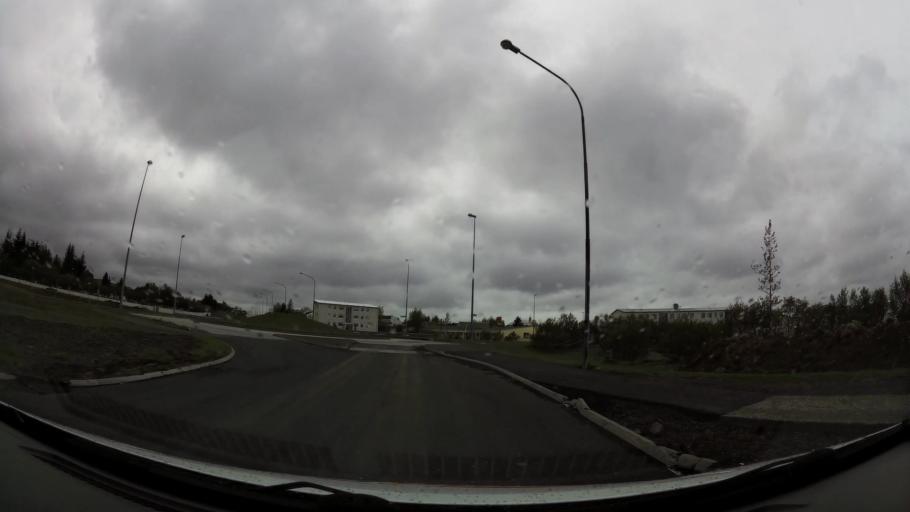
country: IS
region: Capital Region
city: Hafnarfjoerdur
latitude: 64.0626
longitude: -21.9425
